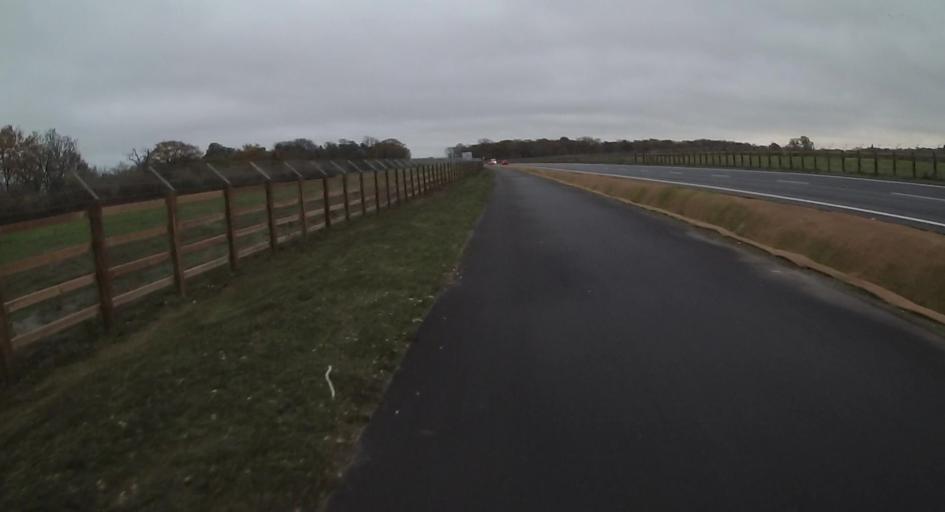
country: GB
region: England
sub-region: West Berkshire
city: Arborfield
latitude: 51.3955
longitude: -0.9202
